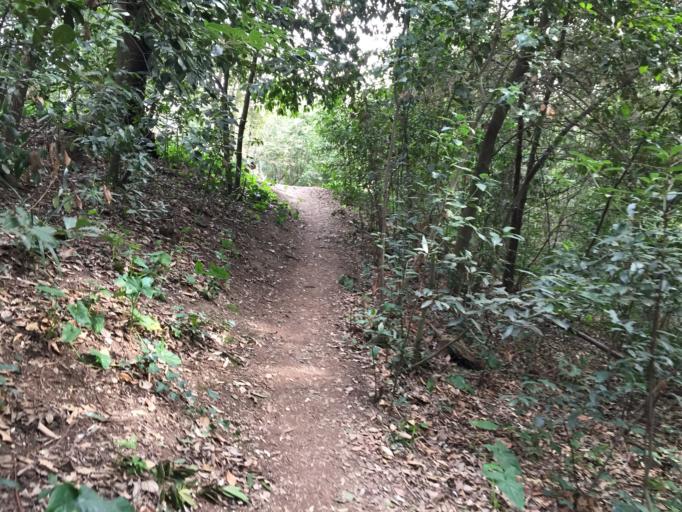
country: VA
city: Vatican City
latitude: 41.8842
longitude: 12.4456
